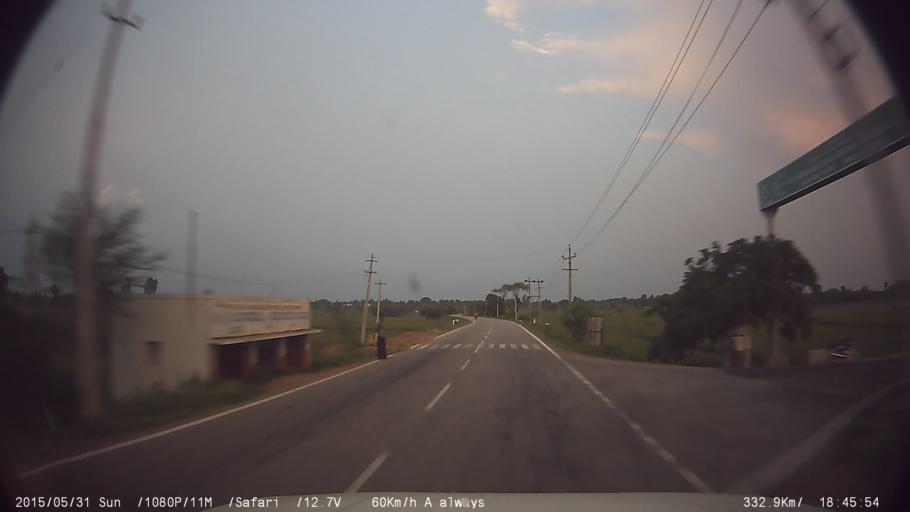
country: IN
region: Karnataka
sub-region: Mysore
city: Tirumakudal Narsipur
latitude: 12.1594
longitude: 76.8287
